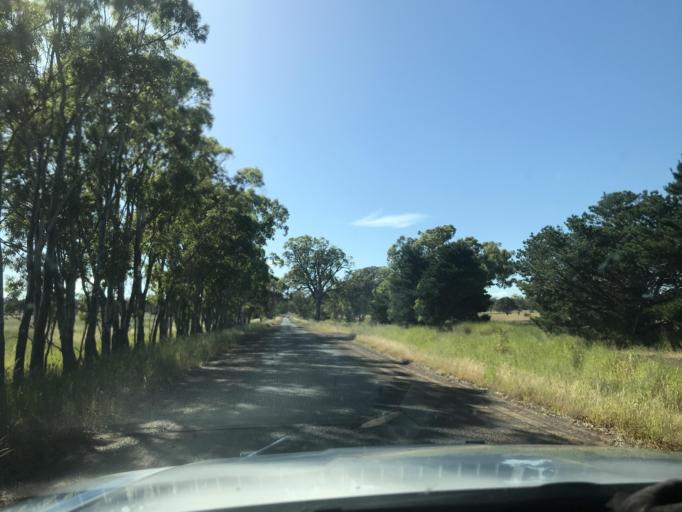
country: AU
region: Victoria
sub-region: Horsham
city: Horsham
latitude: -37.0895
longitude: 141.7646
